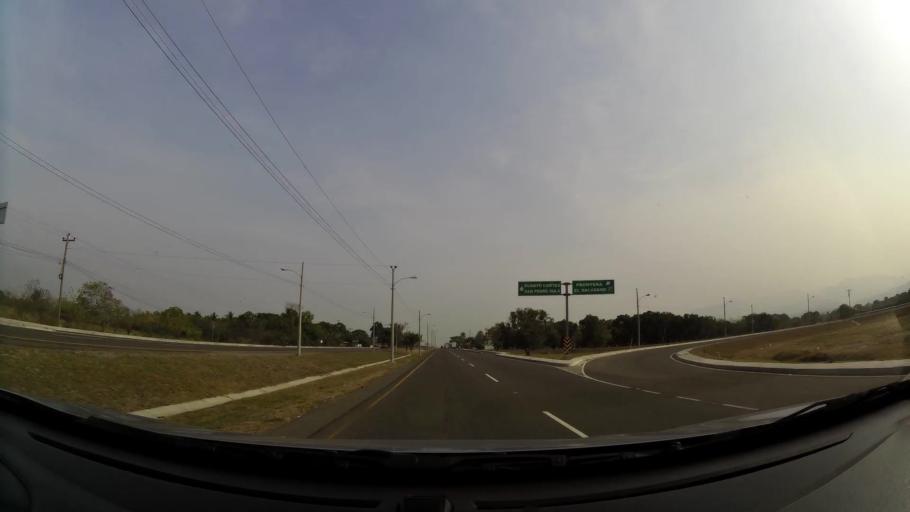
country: HN
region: Comayagua
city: Villa de San Antonio
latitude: 14.3188
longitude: -87.5830
